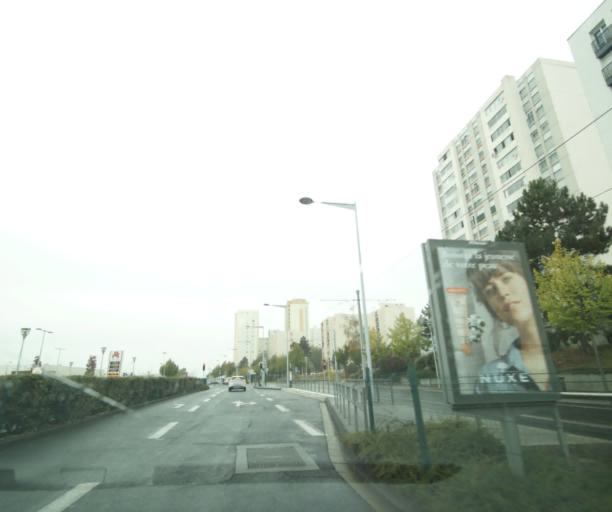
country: FR
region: Auvergne
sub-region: Departement du Puy-de-Dome
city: Cebazat
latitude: 45.8142
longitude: 3.1070
